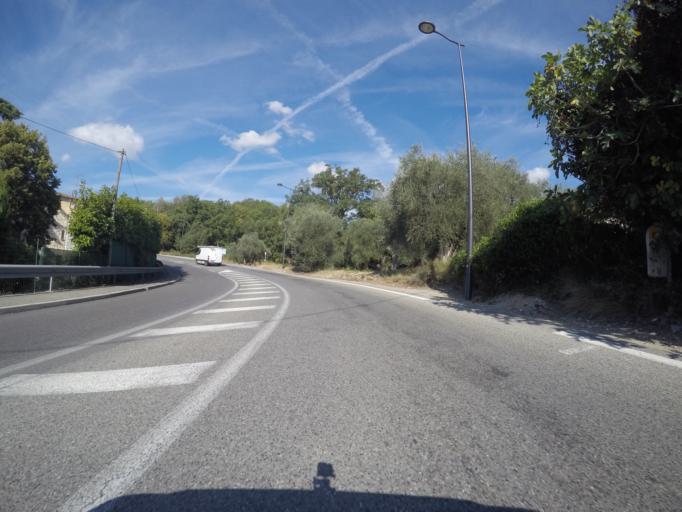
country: FR
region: Provence-Alpes-Cote d'Azur
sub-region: Departement des Alpes-Maritimes
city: La Colle-sur-Loup
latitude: 43.6652
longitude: 7.0649
